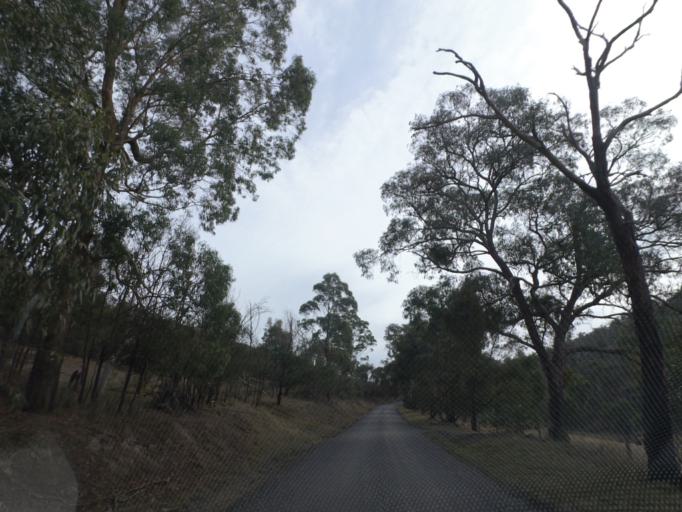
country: AU
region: Victoria
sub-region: Yarra Ranges
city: Yarra Glen
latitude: -37.5968
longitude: 145.3962
